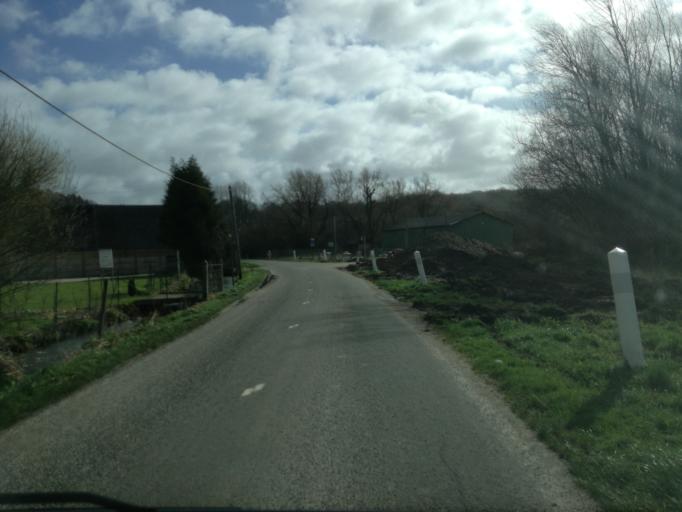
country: FR
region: Haute-Normandie
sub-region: Departement de la Seine-Maritime
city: Bretteville-du-Grand-Caux
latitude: 49.7067
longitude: 0.4325
